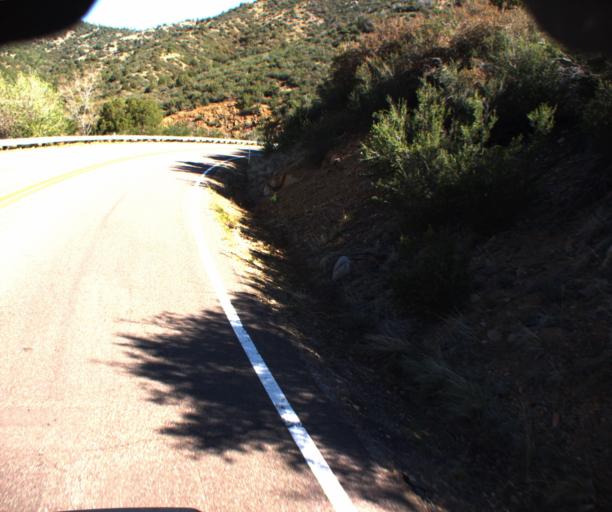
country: US
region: Arizona
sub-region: Yavapai County
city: Prescott
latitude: 34.4739
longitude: -112.5147
